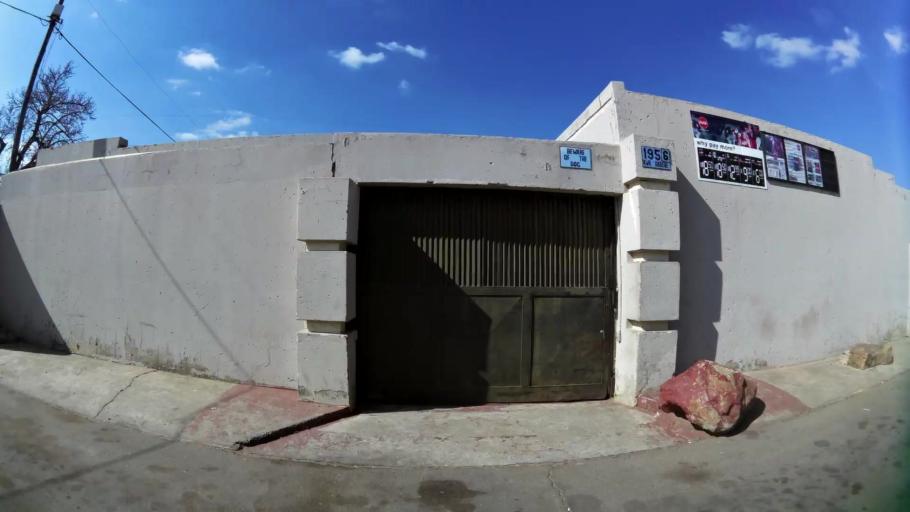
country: ZA
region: Gauteng
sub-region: City of Johannesburg Metropolitan Municipality
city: Soweto
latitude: -26.2543
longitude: 27.8903
